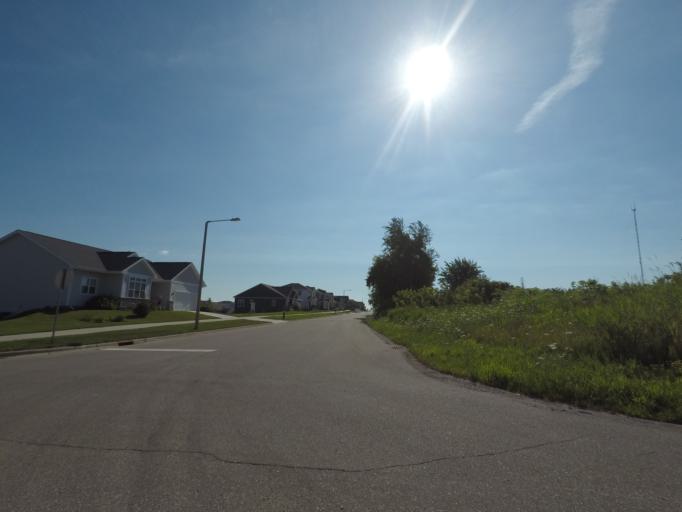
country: US
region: Wisconsin
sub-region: Dane County
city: Middleton
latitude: 43.0639
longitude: -89.5518
